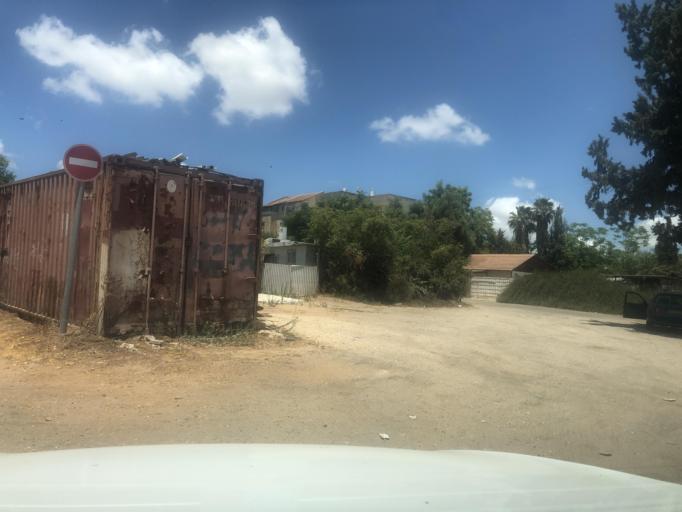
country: IL
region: Central District
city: Kfar Saba
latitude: 32.1589
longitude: 34.9156
